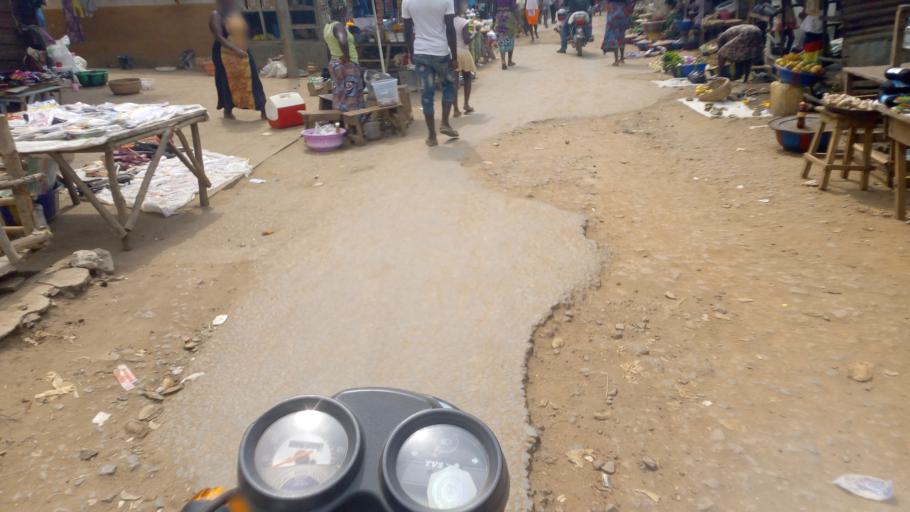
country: SL
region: Western Area
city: Waterloo
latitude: 8.3252
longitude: -13.0663
